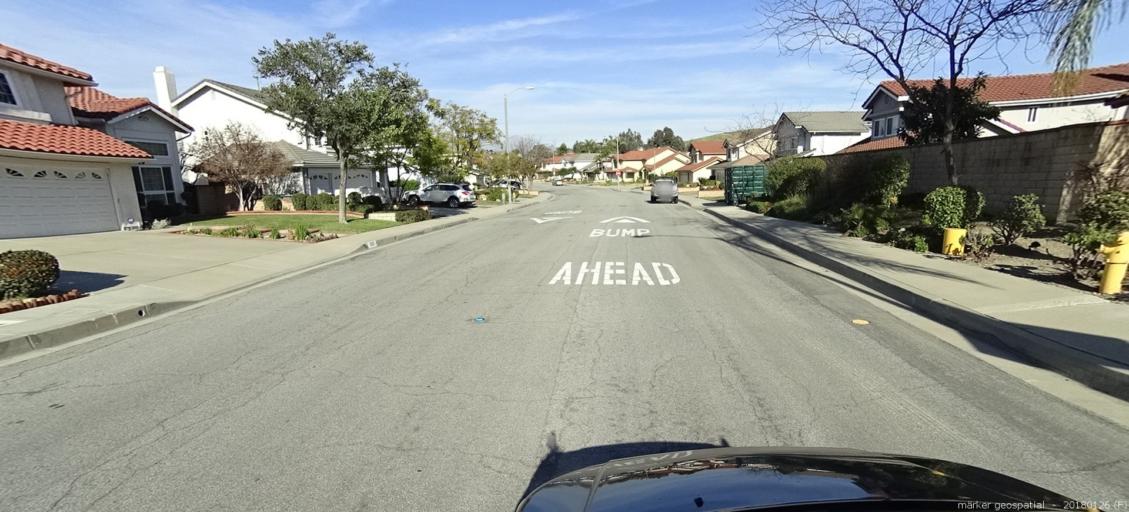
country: US
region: California
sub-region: San Bernardino County
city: Chino Hills
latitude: 33.9980
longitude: -117.7913
